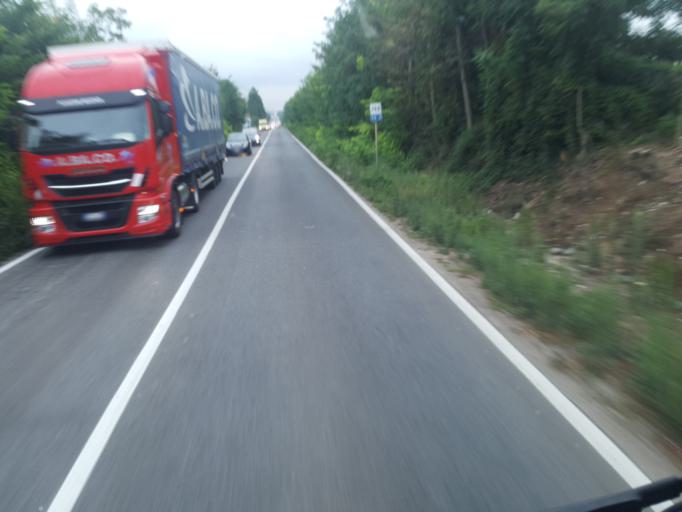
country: IT
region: Campania
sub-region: Provincia di Caserta
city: Pignataro Maggiore
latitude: 41.1691
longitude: 14.1477
